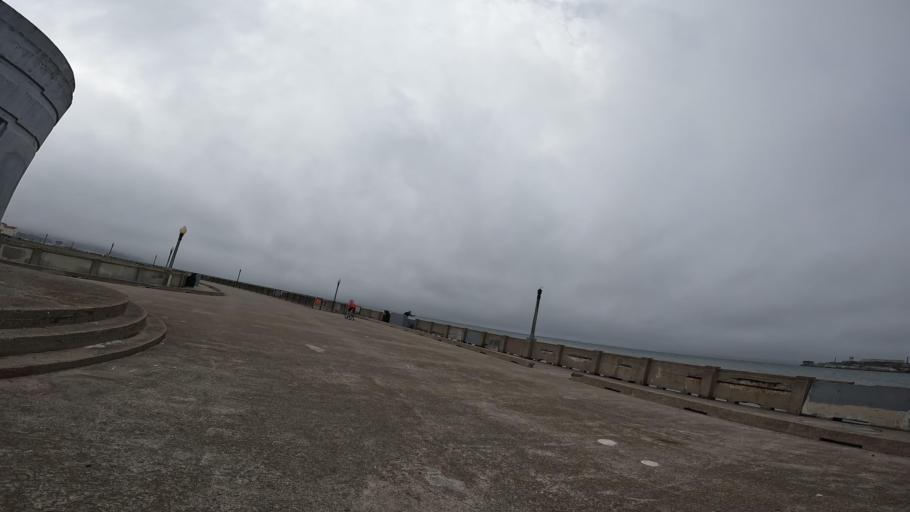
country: US
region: California
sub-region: San Francisco County
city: San Francisco
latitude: 37.8108
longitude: -122.4245
